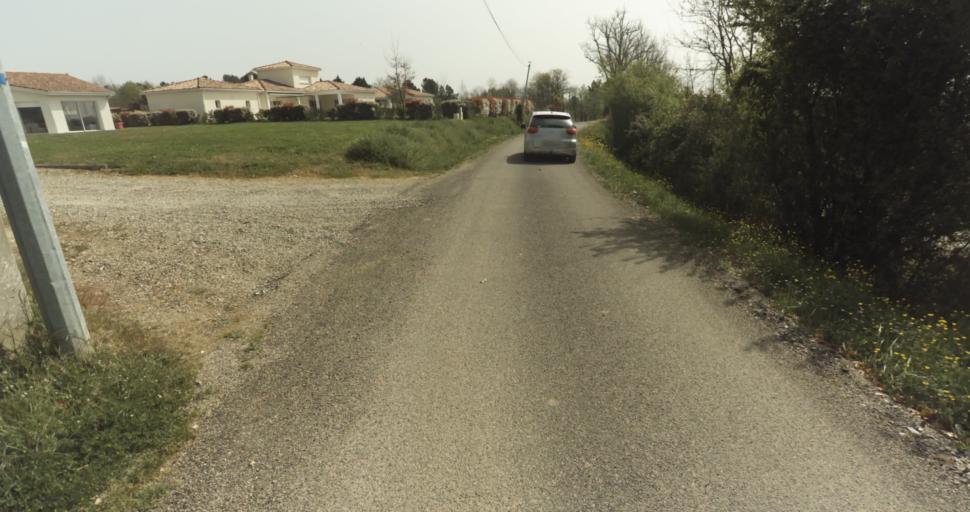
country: FR
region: Midi-Pyrenees
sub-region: Departement du Tarn-et-Garonne
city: Moissac
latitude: 44.1180
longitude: 1.0689
